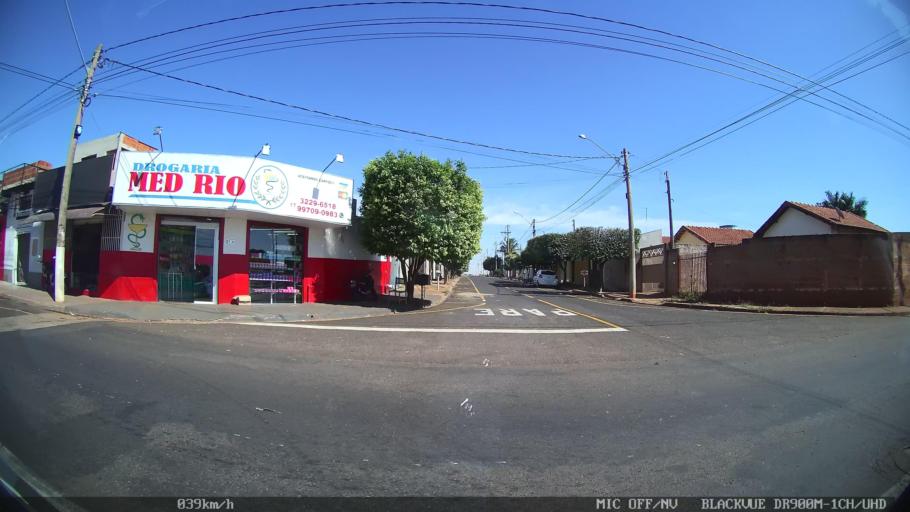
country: BR
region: Sao Paulo
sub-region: Sao Jose Do Rio Preto
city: Sao Jose do Rio Preto
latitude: -20.7472
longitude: -49.4080
